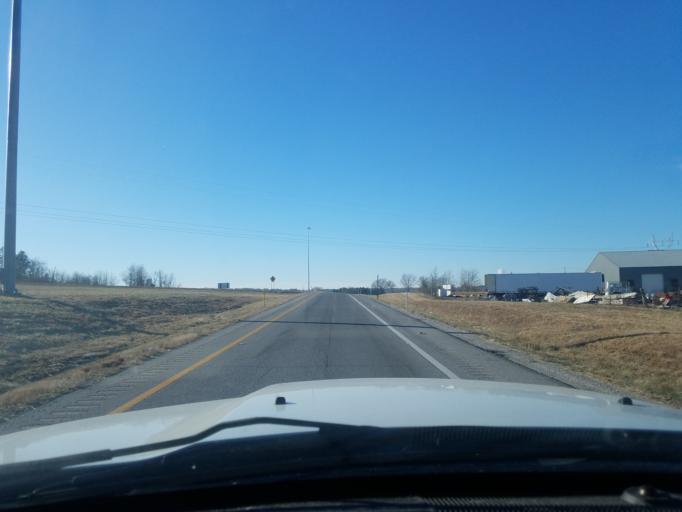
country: US
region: Kentucky
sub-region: Ohio County
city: Beaver Dam
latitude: 37.3678
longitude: -86.8441
